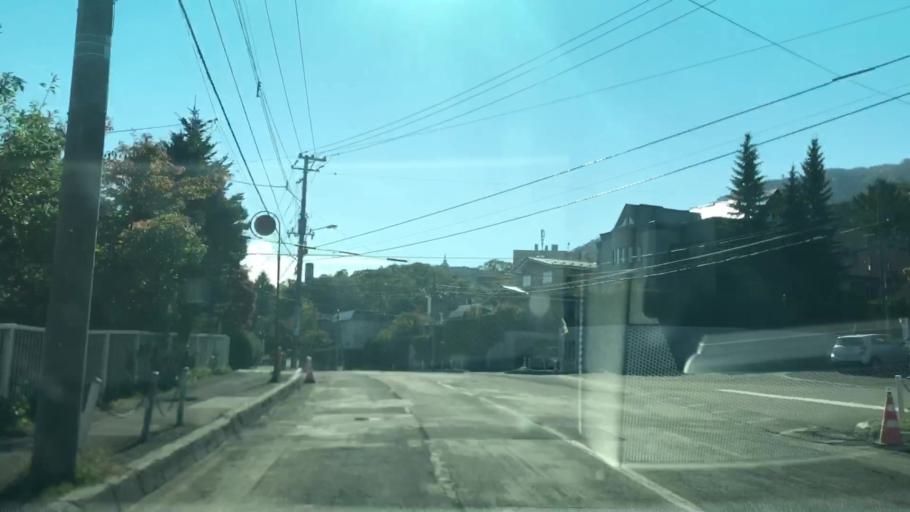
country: JP
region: Hokkaido
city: Sapporo
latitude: 43.0388
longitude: 141.3220
